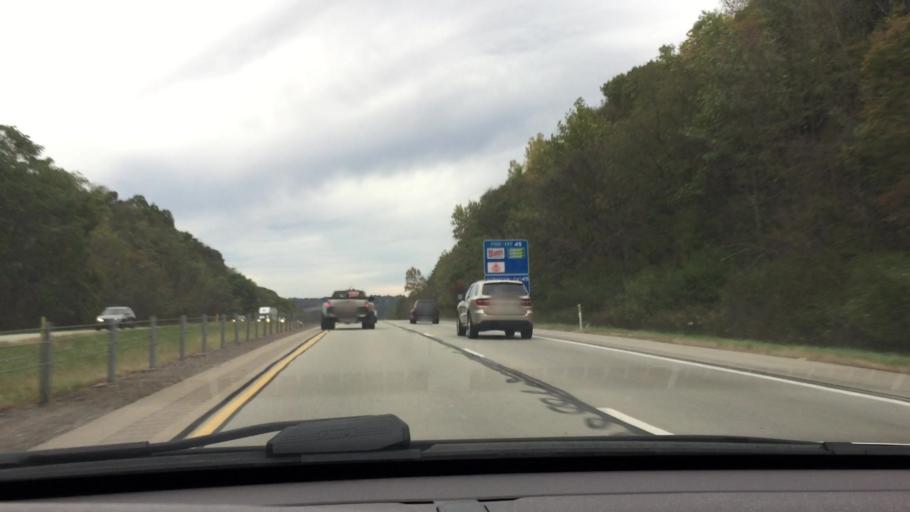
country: US
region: Pennsylvania
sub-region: Beaver County
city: Ambridge
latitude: 40.5882
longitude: -80.2933
